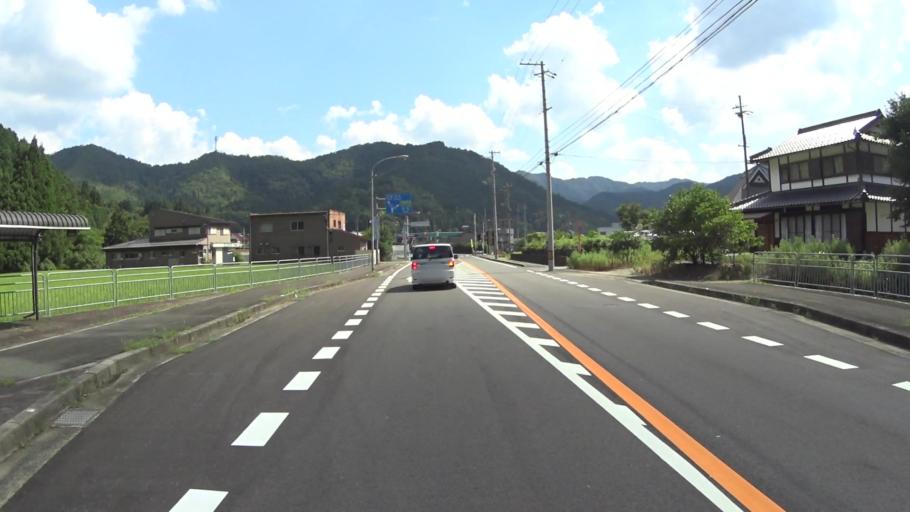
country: JP
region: Kyoto
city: Maizuru
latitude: 35.2805
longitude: 135.5543
